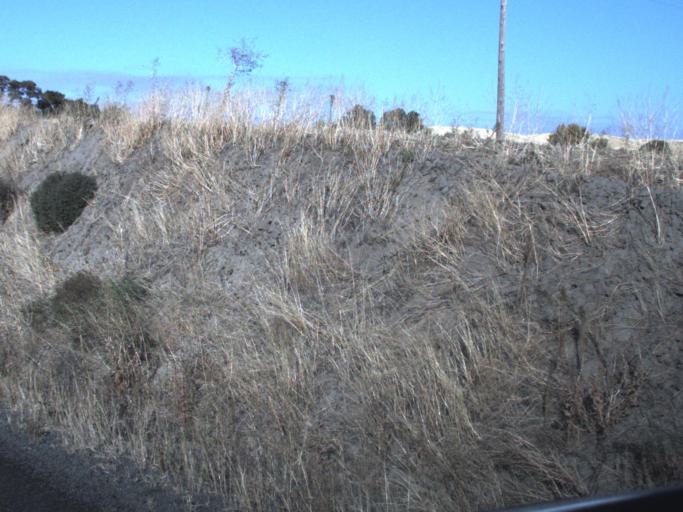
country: US
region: Washington
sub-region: Walla Walla County
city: Walla Walla
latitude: 46.1483
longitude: -118.3726
